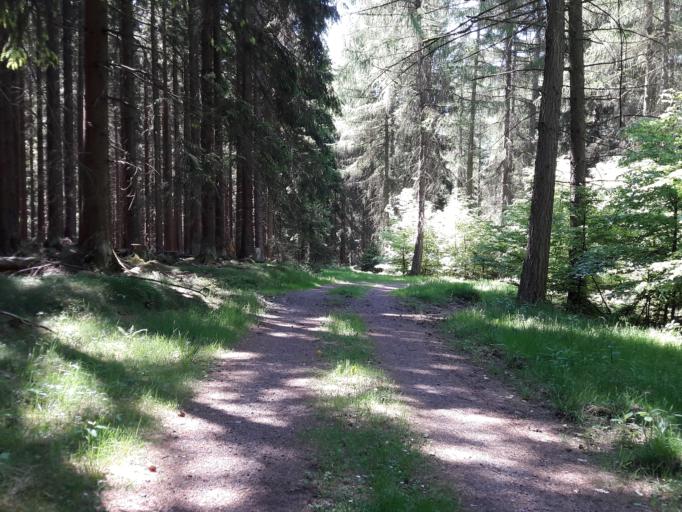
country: DE
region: North Rhine-Westphalia
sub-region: Regierungsbezirk Arnsberg
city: Burbach
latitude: 50.7301
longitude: 8.0832
